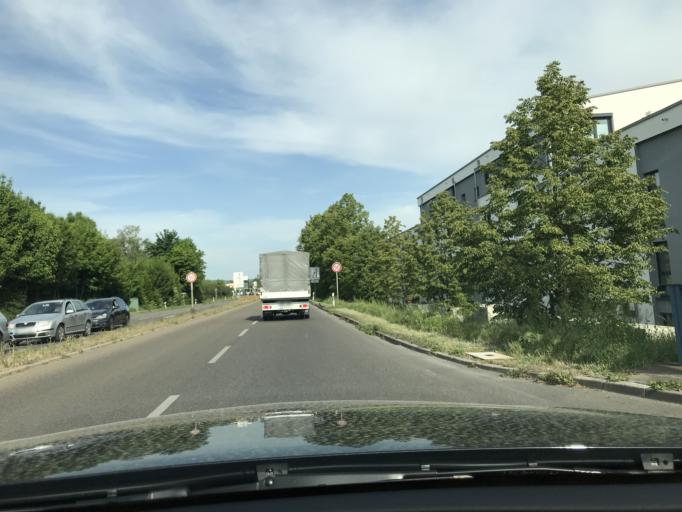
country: DE
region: Baden-Wuerttemberg
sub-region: Regierungsbezirk Stuttgart
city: Waiblingen
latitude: 48.8211
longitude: 9.3072
